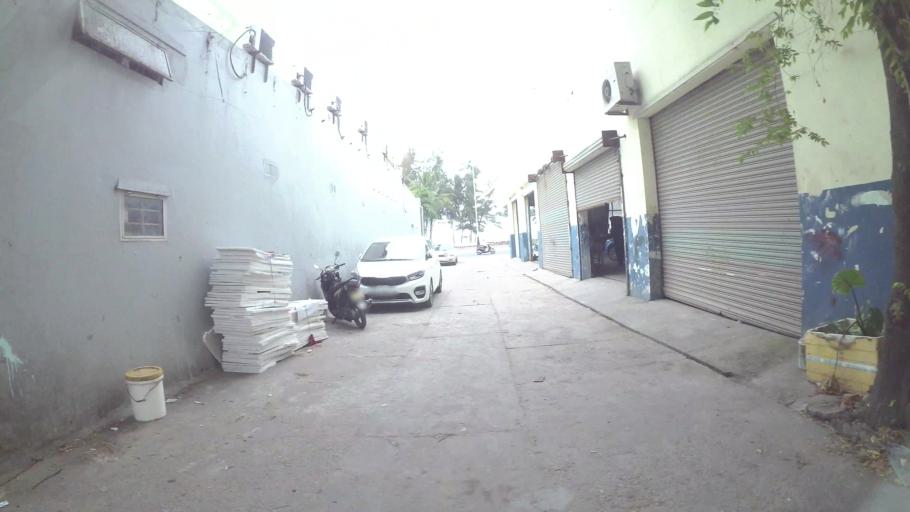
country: VN
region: Da Nang
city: Thanh Khe
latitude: 16.0719
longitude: 108.1963
